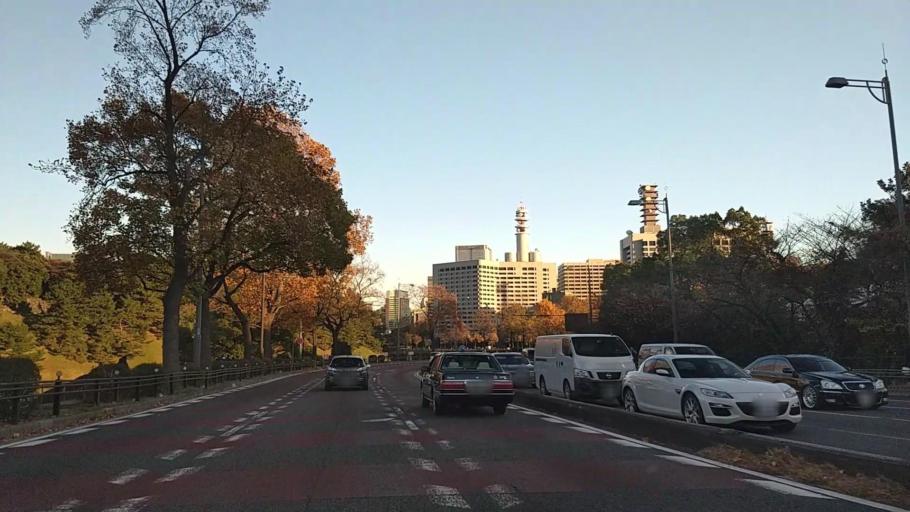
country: JP
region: Tokyo
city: Tokyo
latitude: 35.6797
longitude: 139.7464
